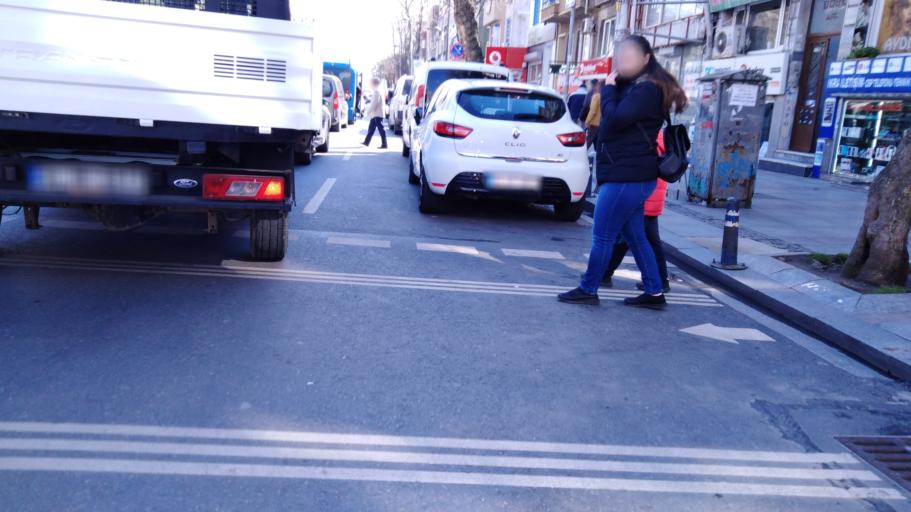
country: TR
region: Istanbul
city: Arikoey
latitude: 41.1691
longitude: 29.0554
